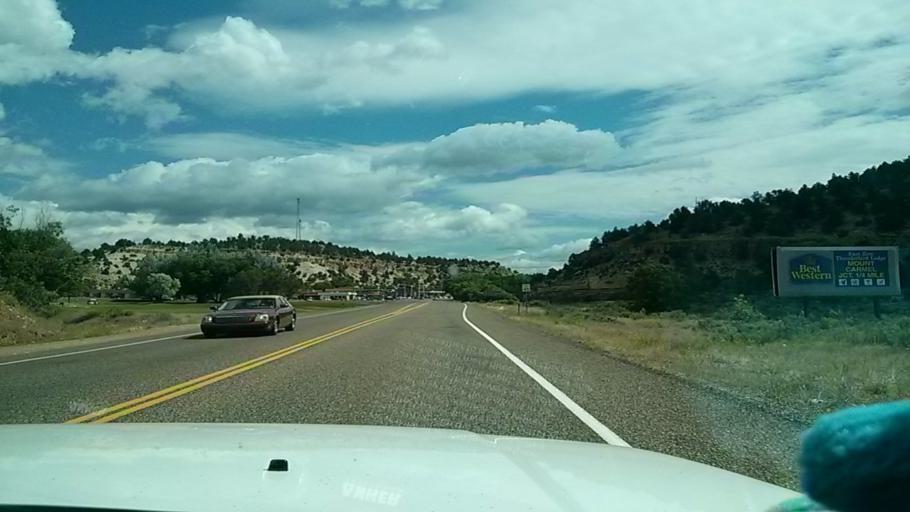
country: US
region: Utah
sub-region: Kane County
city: Kanab
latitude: 37.2193
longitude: -112.6824
